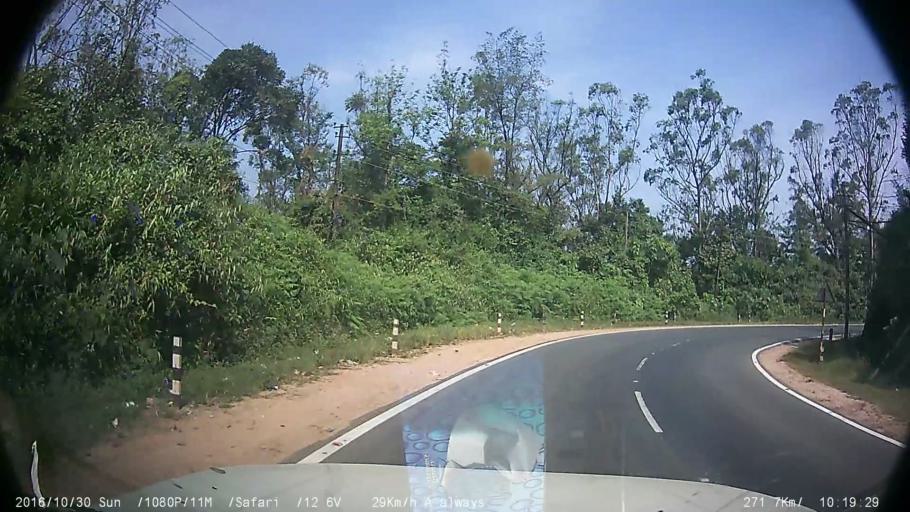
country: IN
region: Karnataka
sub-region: Kodagu
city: Madikeri
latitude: 12.4261
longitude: 75.7528
